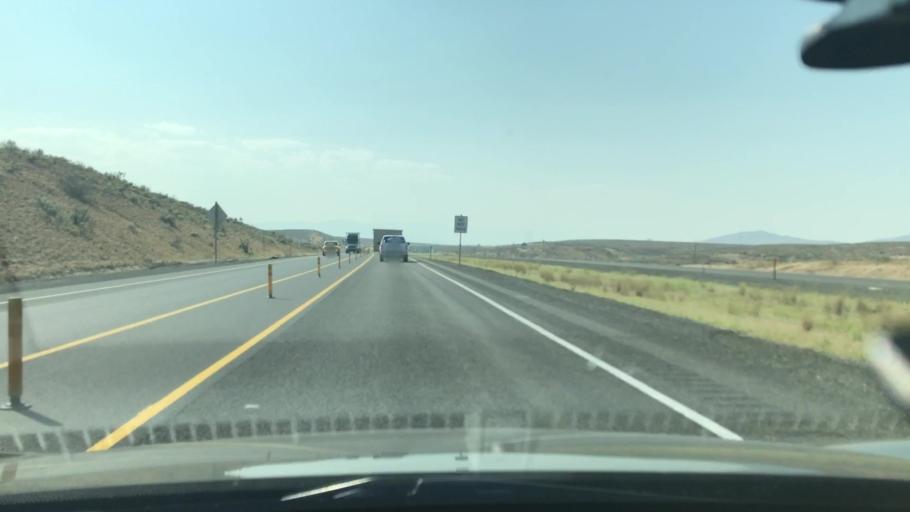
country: US
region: Oregon
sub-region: Baker County
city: Baker City
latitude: 44.6852
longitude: -117.6673
